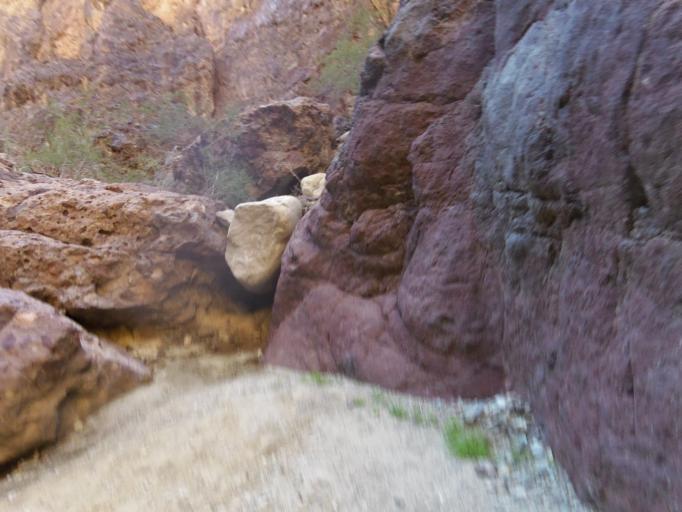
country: US
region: Nevada
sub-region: Clark County
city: Boulder City
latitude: 35.9699
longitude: -114.7179
